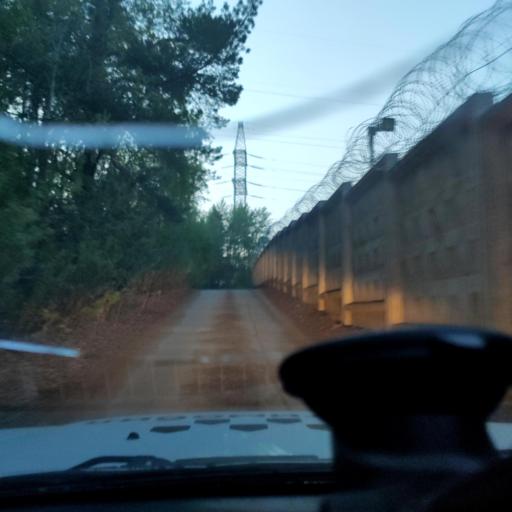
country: RU
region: Perm
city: Perm
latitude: 58.1133
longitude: 56.3426
